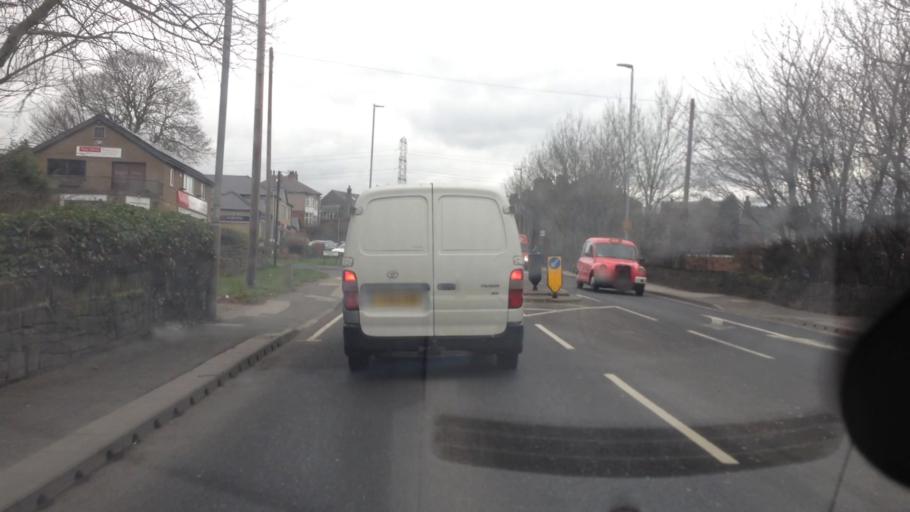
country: GB
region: England
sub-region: Calderdale
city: Elland
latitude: 53.6666
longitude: -1.8229
